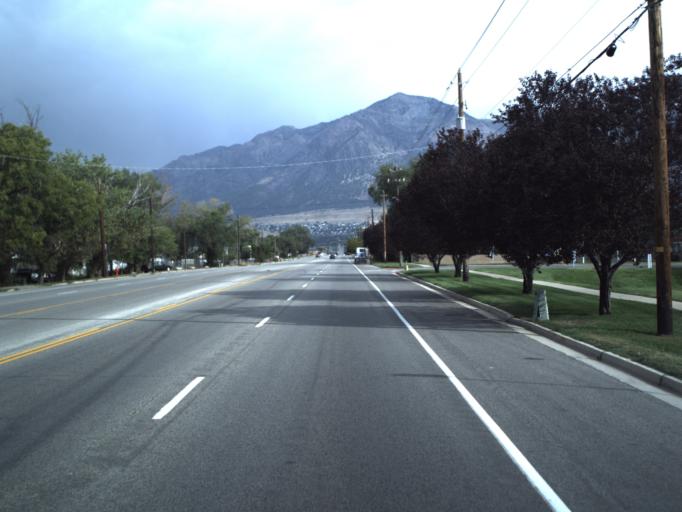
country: US
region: Utah
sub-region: Weber County
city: Harrisville
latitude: 41.2833
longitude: -111.9691
